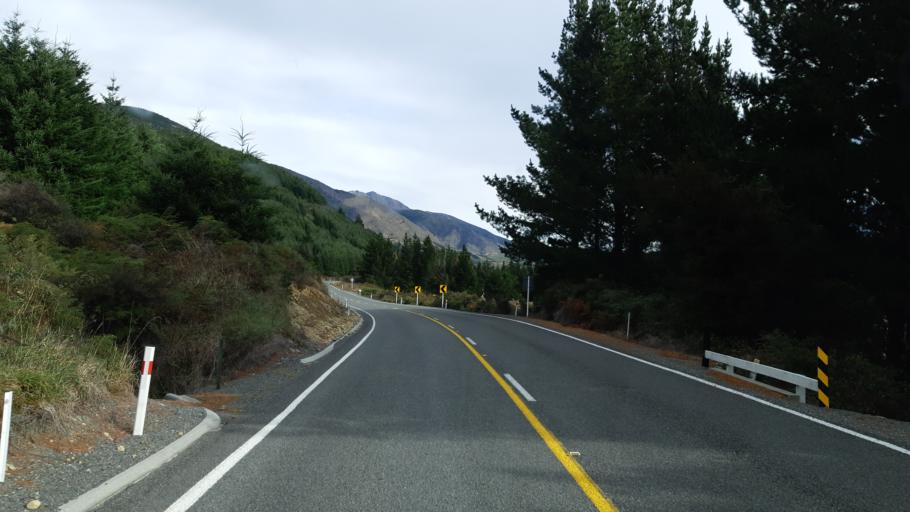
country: NZ
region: Tasman
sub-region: Tasman District
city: Wakefield
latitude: -41.7019
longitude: 173.1273
